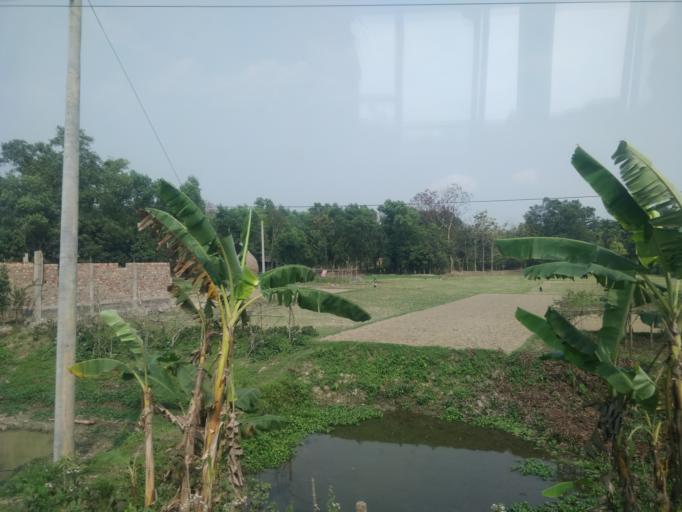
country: BD
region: Sylhet
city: Habiganj
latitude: 24.3260
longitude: 91.4328
